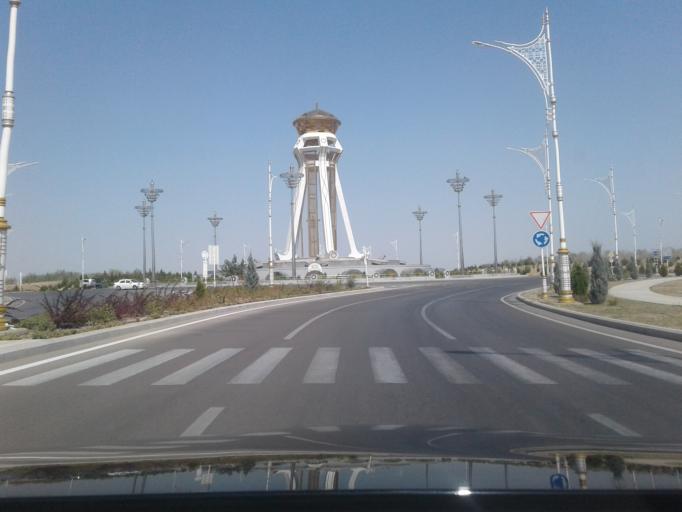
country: TM
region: Ahal
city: Ashgabat
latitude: 37.8780
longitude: 58.4208
